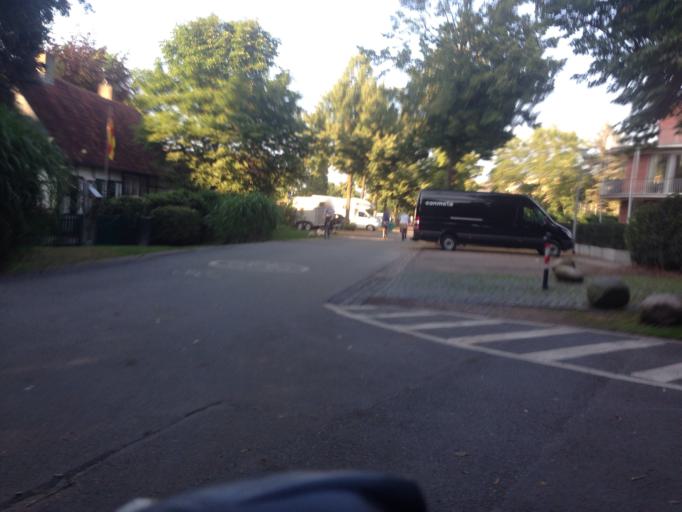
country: DE
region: North Rhine-Westphalia
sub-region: Regierungsbezirk Munster
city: Muenster
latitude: 51.9550
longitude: 7.6062
